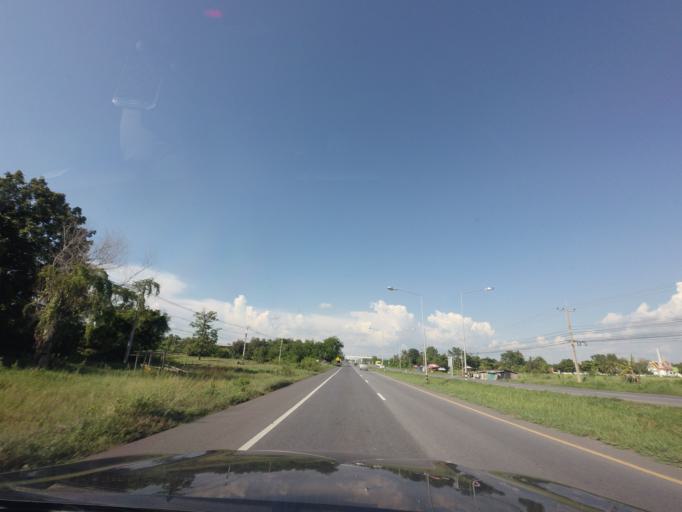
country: TH
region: Khon Kaen
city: Non Sila
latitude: 15.9487
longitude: 102.6818
